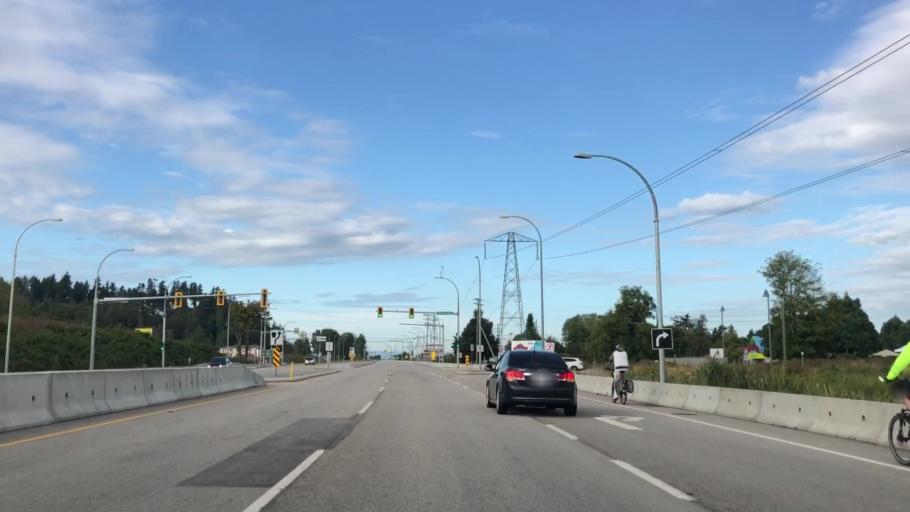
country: US
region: Washington
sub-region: Whatcom County
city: Point Roberts
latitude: 49.0332
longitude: -123.0890
